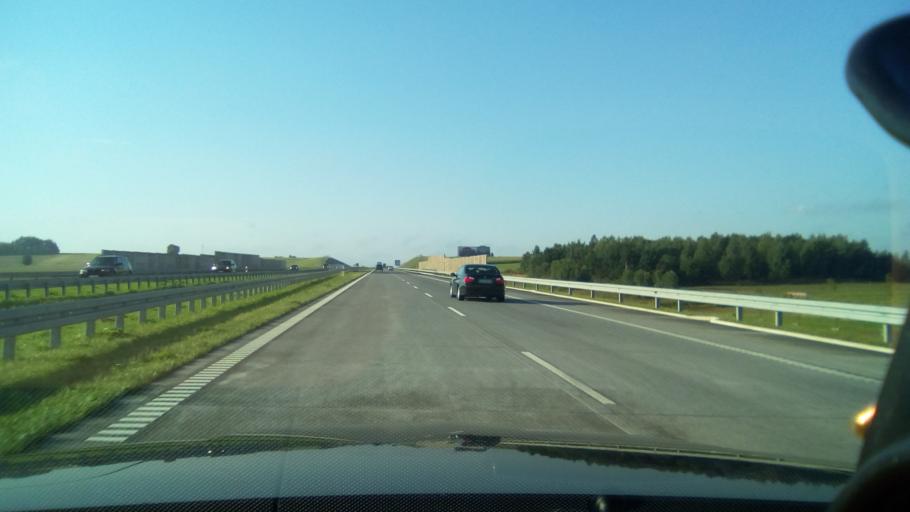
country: PL
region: Silesian Voivodeship
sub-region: Powiat czestochowski
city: Starcza
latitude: 50.6272
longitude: 19.0333
